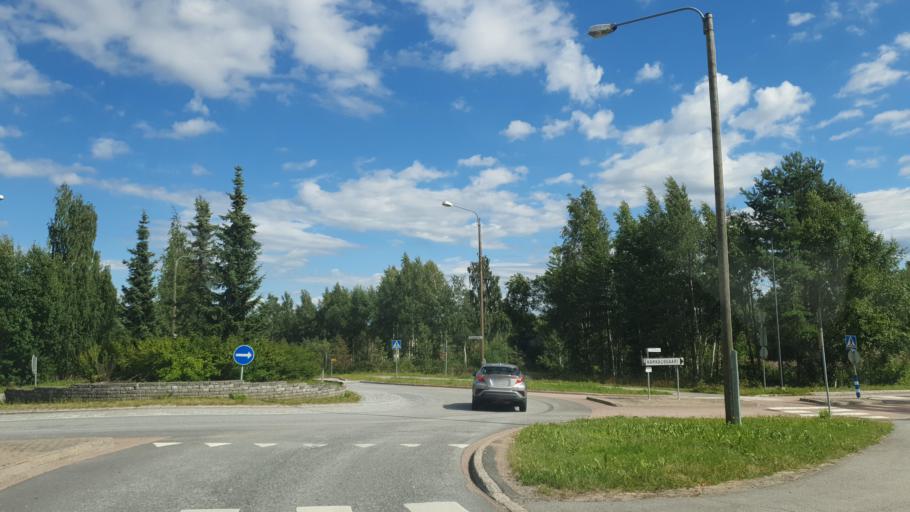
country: FI
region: Central Finland
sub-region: Jyvaeskylae
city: Saeynaetsalo
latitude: 62.1374
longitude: 25.7343
